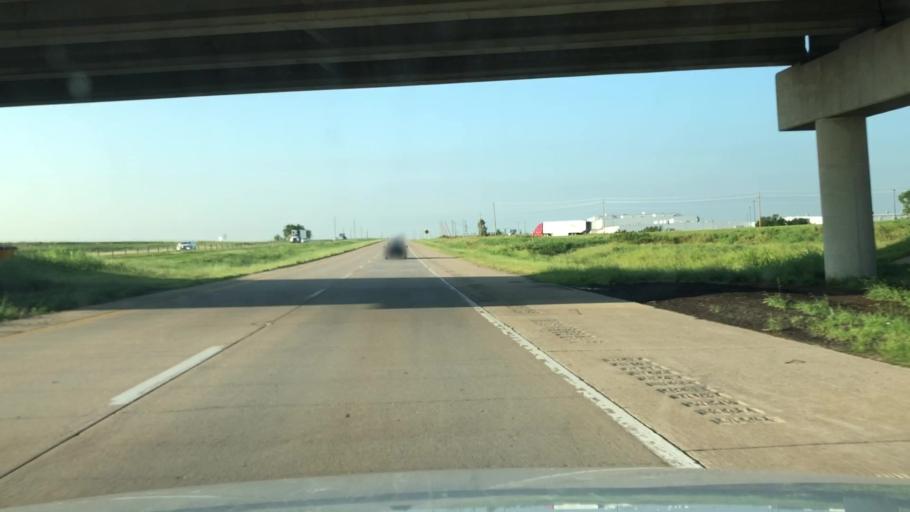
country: US
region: Oklahoma
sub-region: Washington County
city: Bartlesville
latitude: 36.5833
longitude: -95.9311
